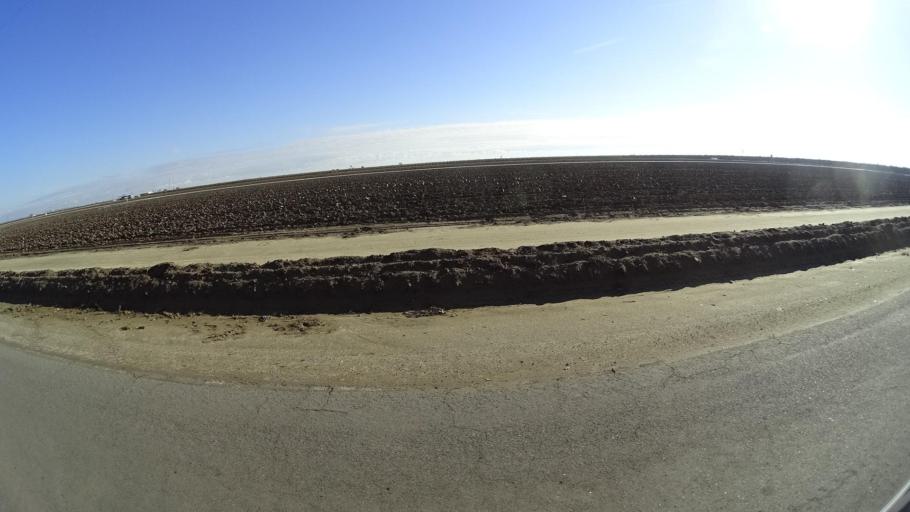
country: US
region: California
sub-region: Kern County
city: McFarland
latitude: 35.6985
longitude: -119.2942
